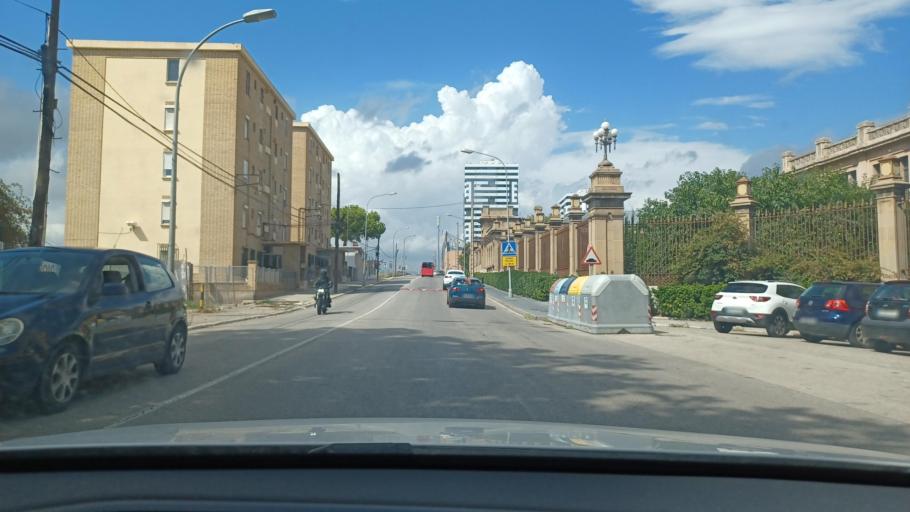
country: ES
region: Catalonia
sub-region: Provincia de Tarragona
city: Tarragona
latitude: 41.1143
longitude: 1.2383
